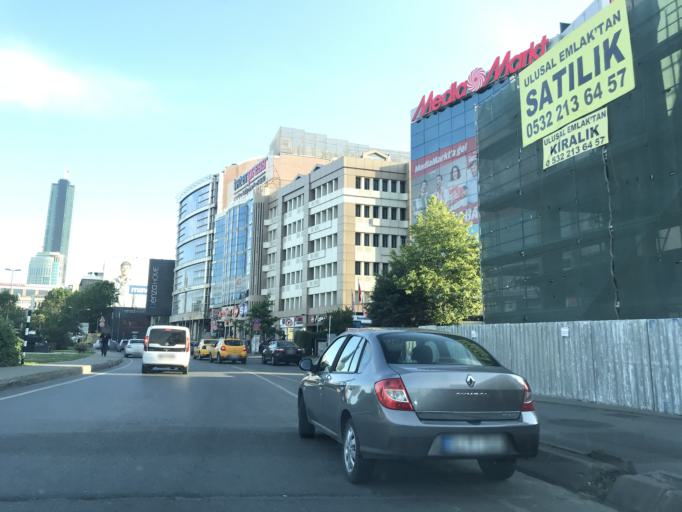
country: TR
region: Istanbul
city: Sisli
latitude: 41.0932
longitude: 29.0046
